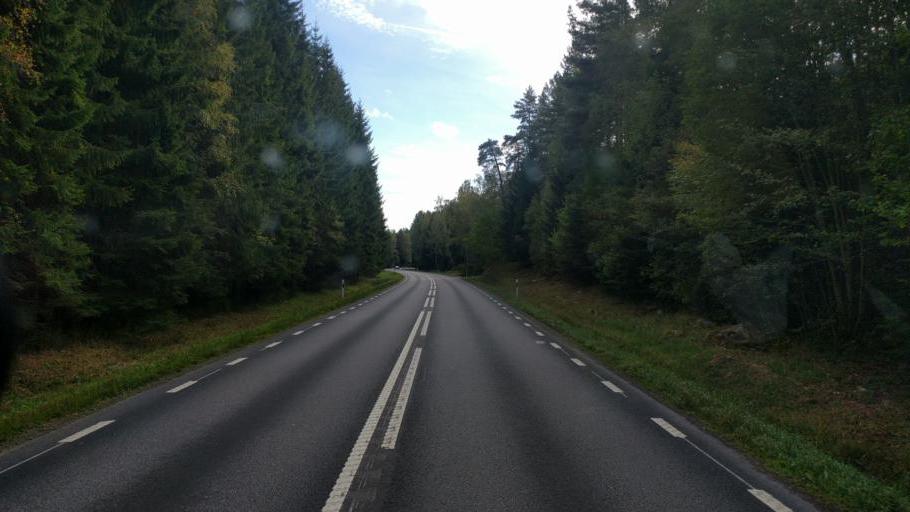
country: SE
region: OEstergoetland
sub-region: Kinda Kommun
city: Kisa
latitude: 57.9667
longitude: 15.6548
